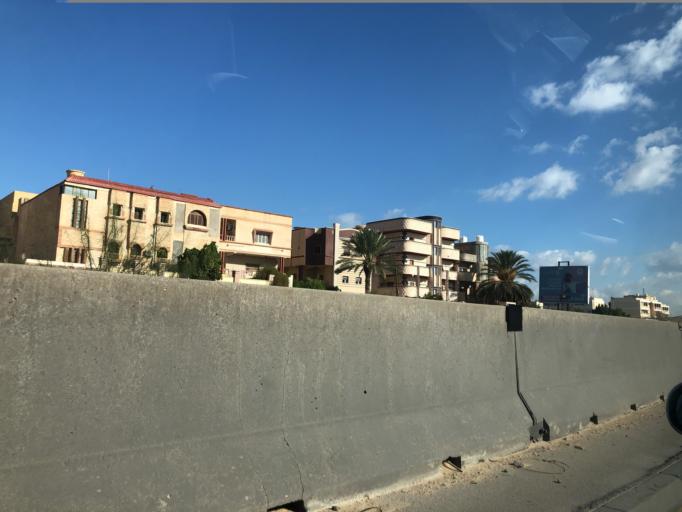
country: LY
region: Tripoli
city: Tripoli
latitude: 32.8568
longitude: 13.2069
